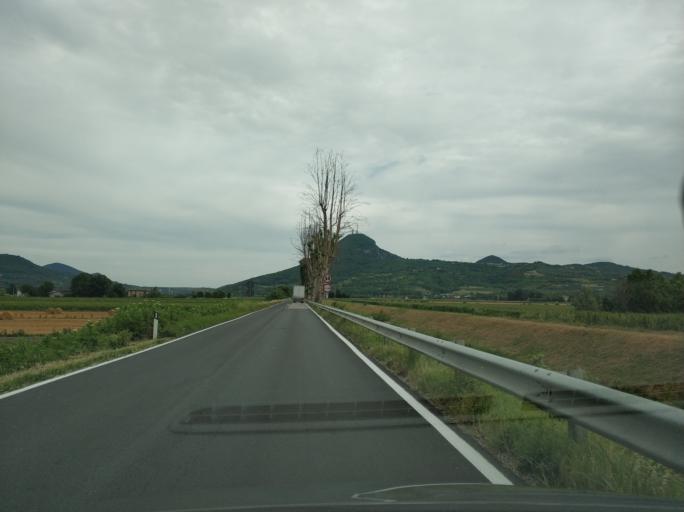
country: IT
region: Veneto
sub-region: Provincia di Padova
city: Lozzo Atestino
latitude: 45.2626
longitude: 11.6272
